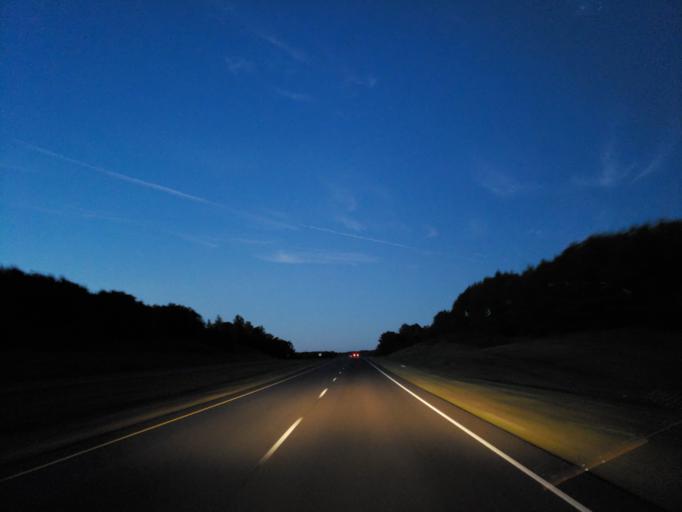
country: US
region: Mississippi
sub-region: Clarke County
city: Quitman
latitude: 32.0260
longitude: -88.6832
